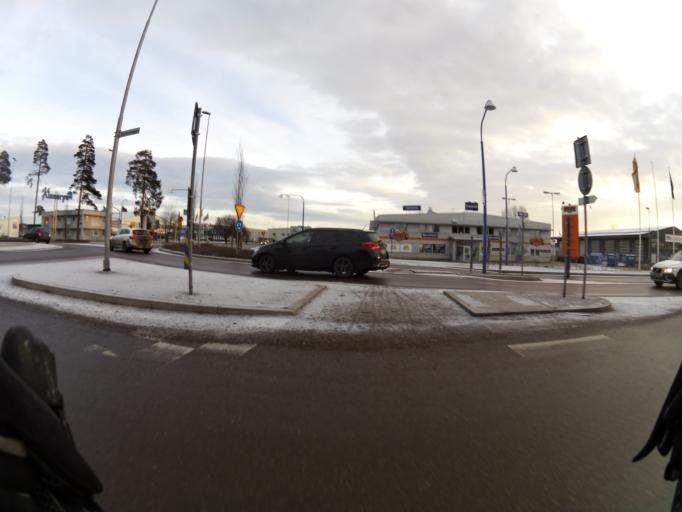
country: SE
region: Gaevleborg
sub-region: Gavle Kommun
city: Gavle
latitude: 60.6616
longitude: 17.1770
